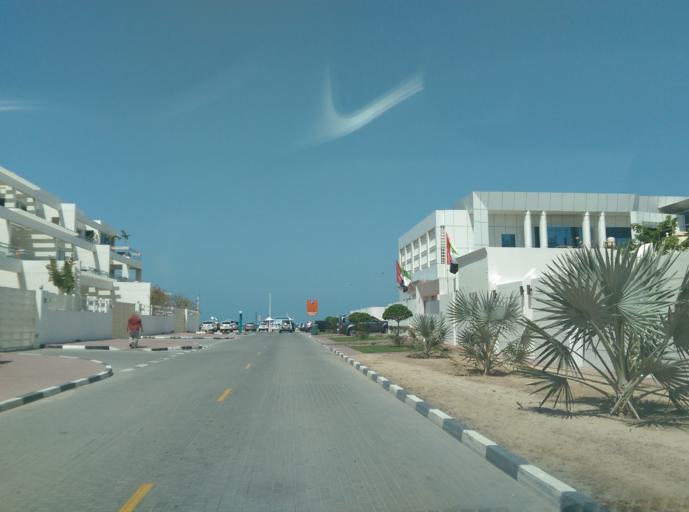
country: AE
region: Dubai
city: Dubai
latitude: 25.1851
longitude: 55.2262
